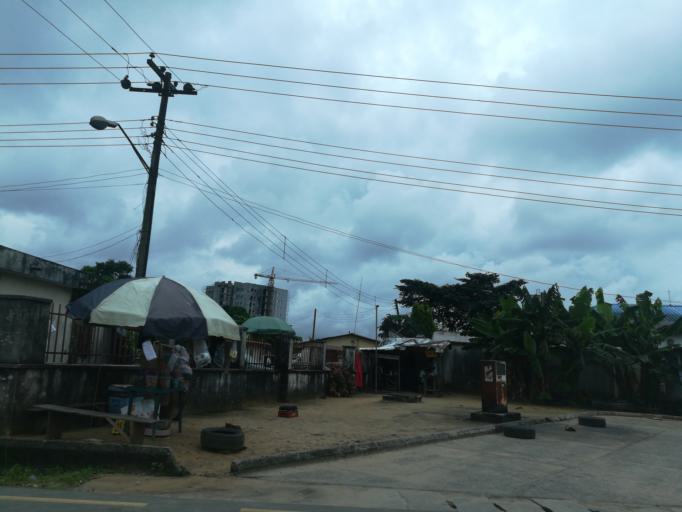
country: NG
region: Rivers
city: Port Harcourt
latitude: 4.7700
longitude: 7.0190
